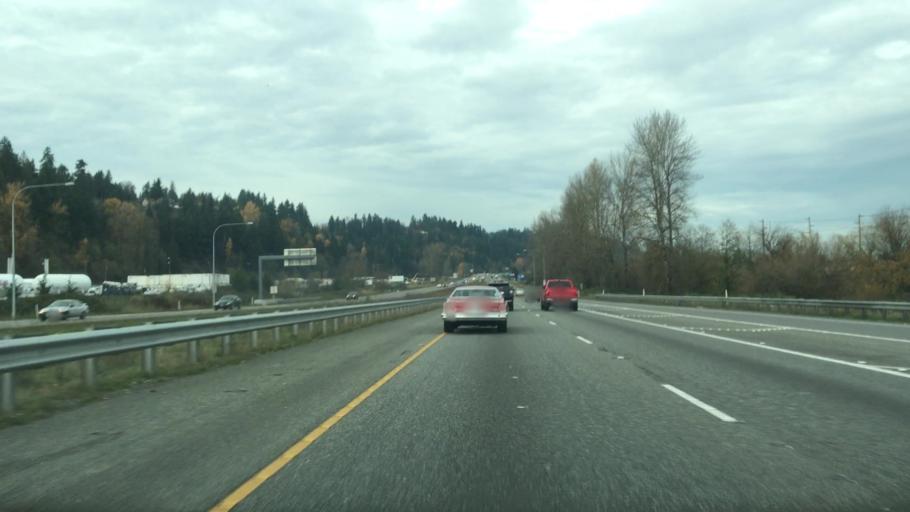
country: US
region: Washington
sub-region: King County
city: Pacific
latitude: 47.2536
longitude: -122.2582
